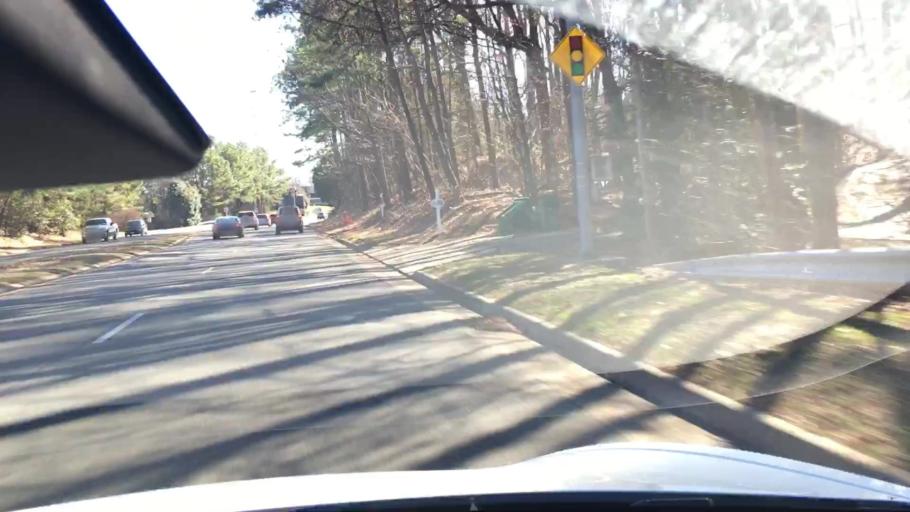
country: US
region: Virginia
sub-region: Henrico County
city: Tuckahoe
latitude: 37.5838
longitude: -77.5699
